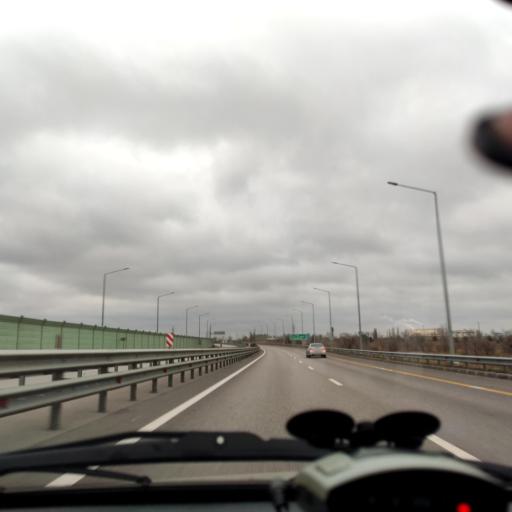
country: RU
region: Voronezj
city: Novaya Usman'
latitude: 51.6361
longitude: 39.3171
